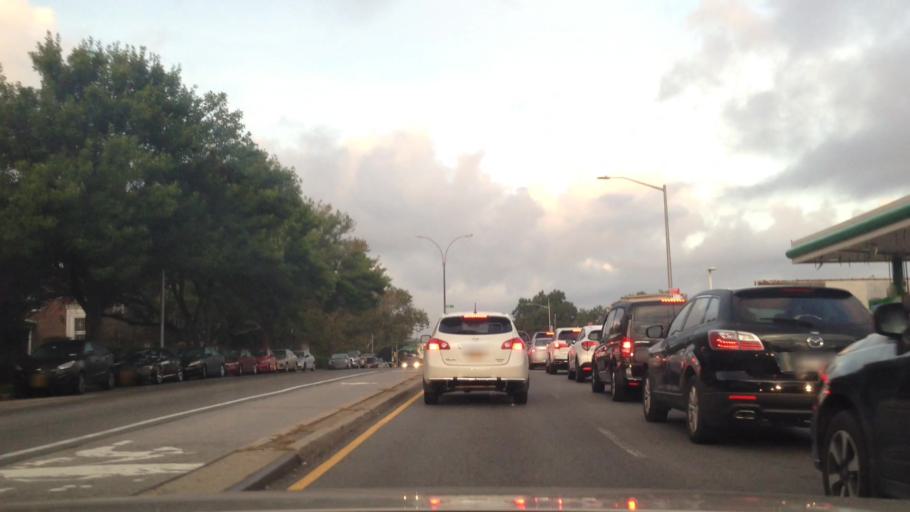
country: US
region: New York
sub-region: Queens County
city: Jamaica
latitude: 40.7183
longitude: -73.8152
